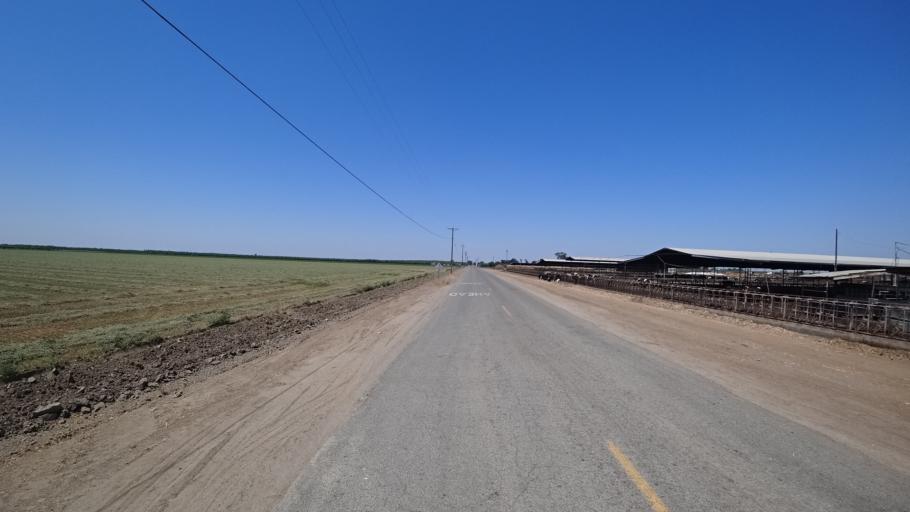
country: US
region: California
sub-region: Kings County
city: Armona
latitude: 36.3572
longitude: -119.7286
